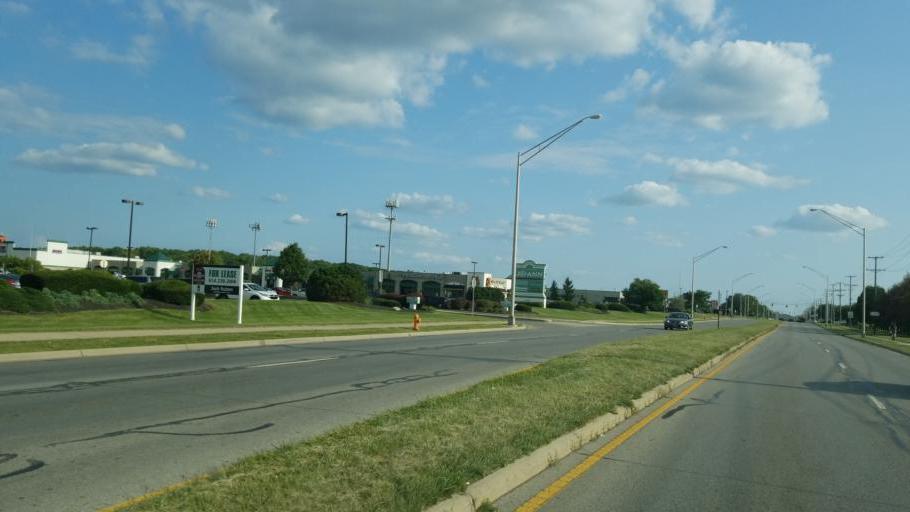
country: US
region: Ohio
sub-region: Franklin County
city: Dublin
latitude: 40.0940
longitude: -83.0917
